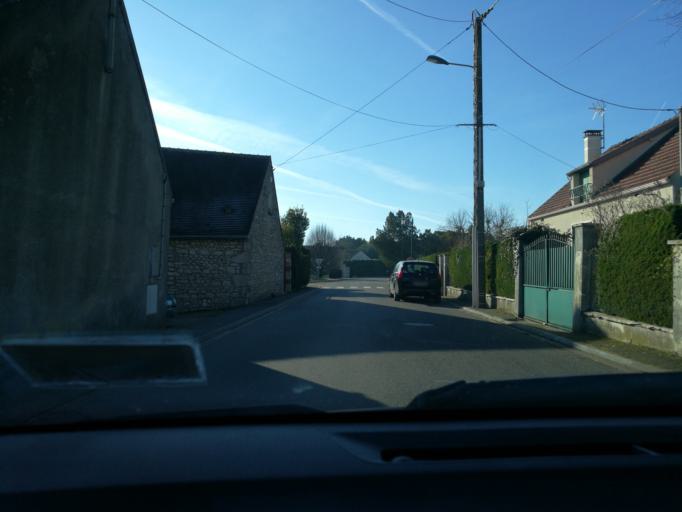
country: FR
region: Centre
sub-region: Departement du Loiret
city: Chaingy
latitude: 47.8797
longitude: 1.7717
